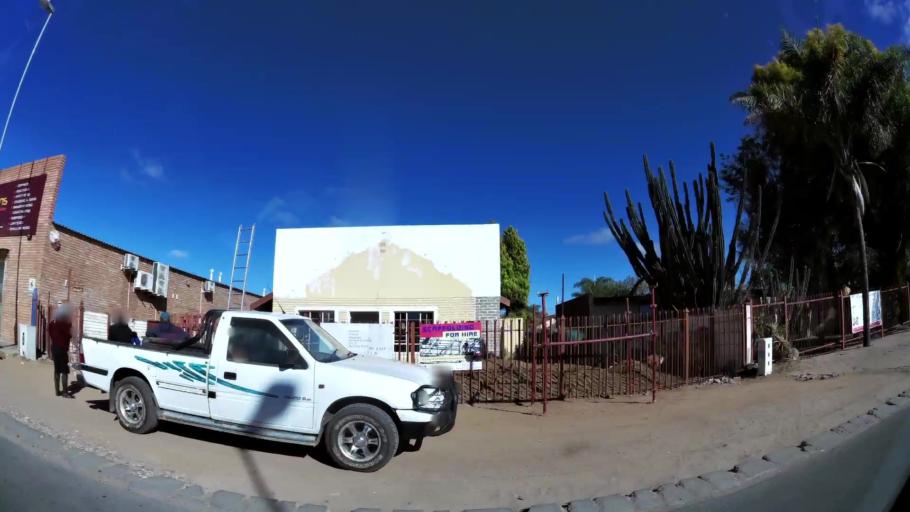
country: ZA
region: Limpopo
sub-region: Capricorn District Municipality
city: Polokwane
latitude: -23.9181
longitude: 29.4517
